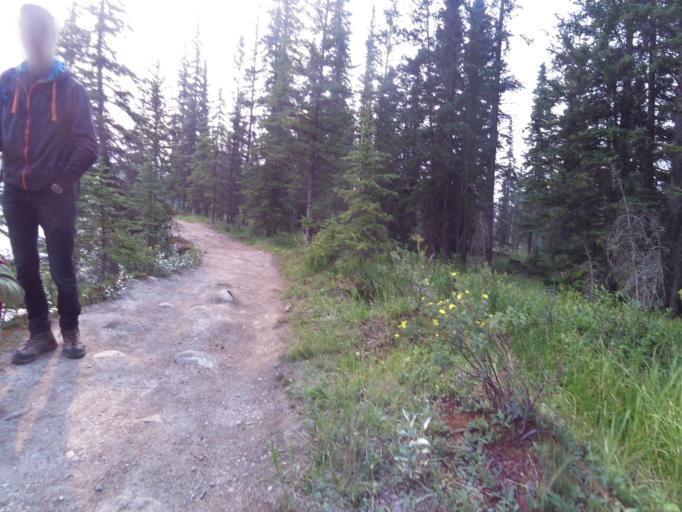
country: CA
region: Alberta
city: Jasper Park Lodge
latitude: 52.8804
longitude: -118.0647
